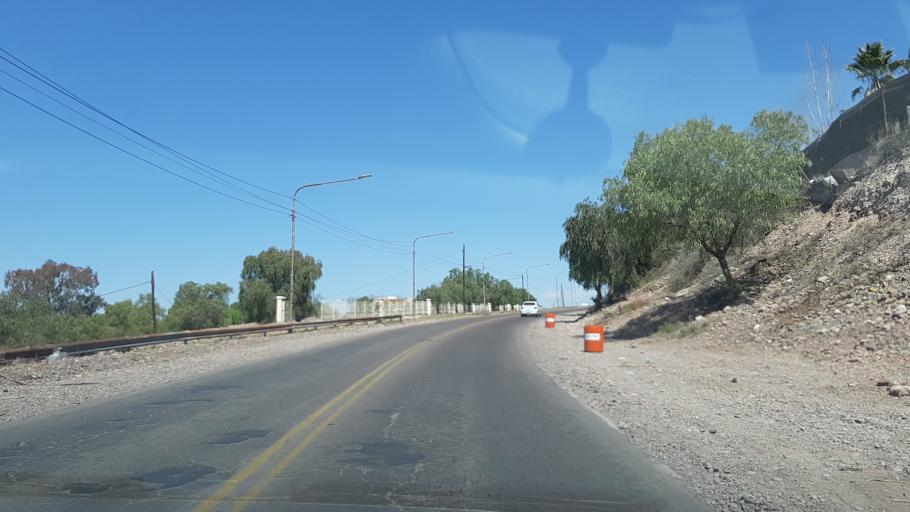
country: AR
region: Mendoza
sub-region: Departamento de Godoy Cruz
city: Godoy Cruz
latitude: -32.9648
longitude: -68.8722
